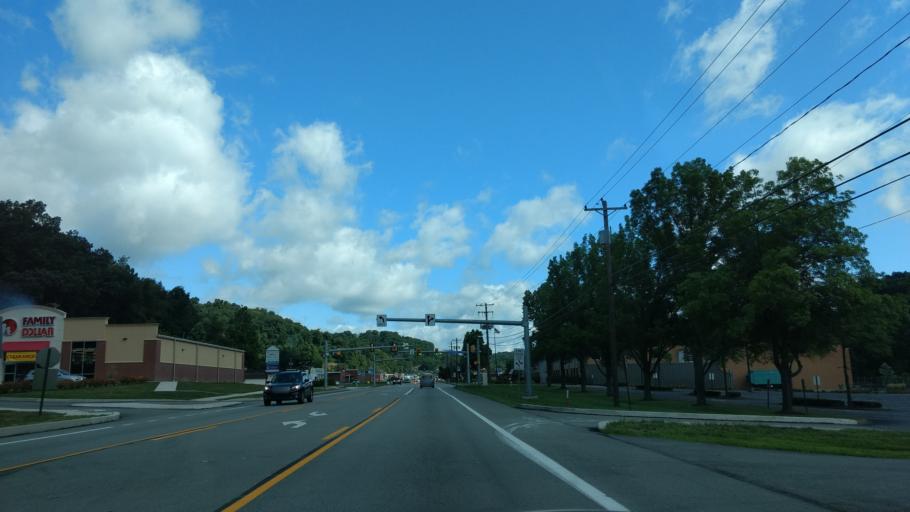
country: US
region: Pennsylvania
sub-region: Westmoreland County
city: Murrysville
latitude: 40.4413
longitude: -79.7132
